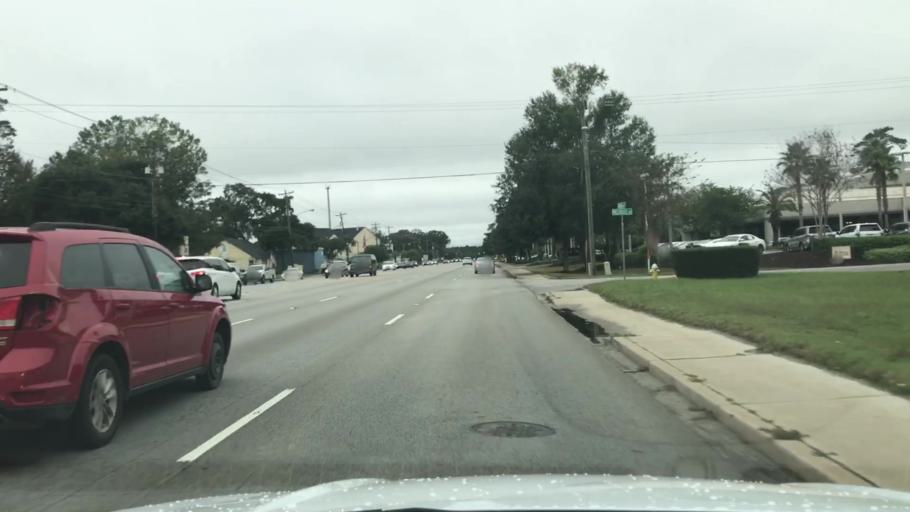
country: US
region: South Carolina
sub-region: Charleston County
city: Shell Point
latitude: 32.7925
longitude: -80.0461
